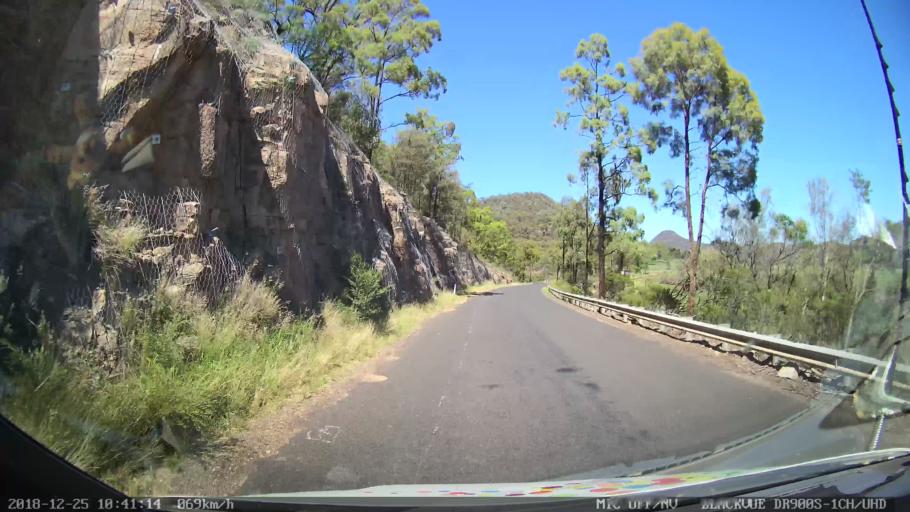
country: AU
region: New South Wales
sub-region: Upper Hunter Shire
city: Merriwa
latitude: -32.4152
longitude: 150.3374
